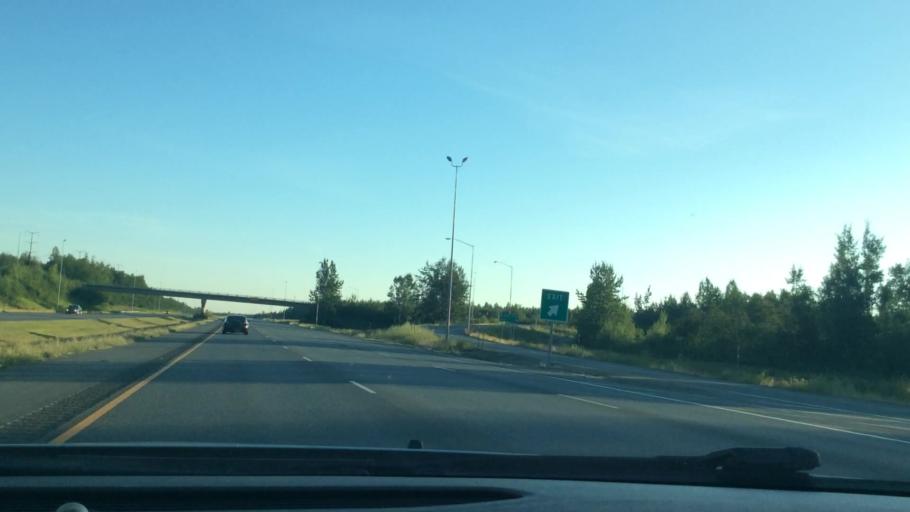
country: US
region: Alaska
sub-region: Anchorage Municipality
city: Elmendorf Air Force Base
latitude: 61.2551
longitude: -149.6553
